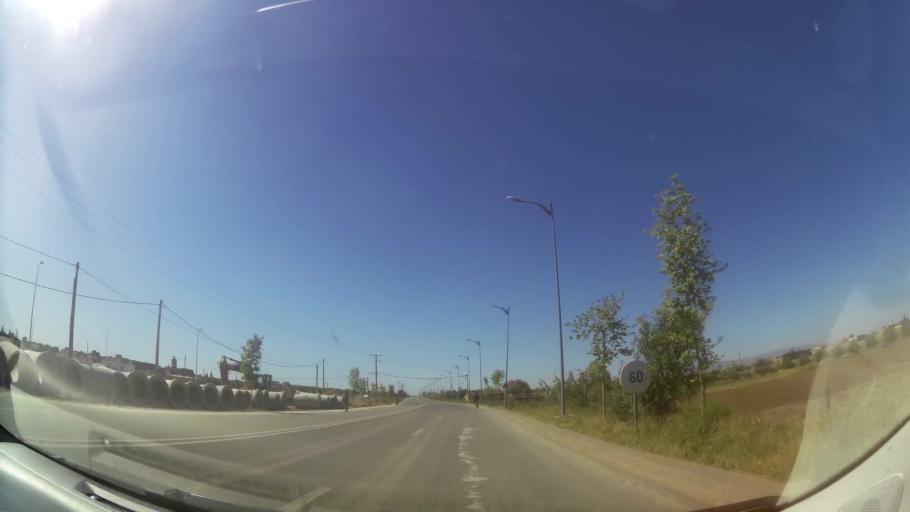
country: MA
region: Oriental
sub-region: Oujda-Angad
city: Oujda
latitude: 34.7194
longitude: -1.8650
